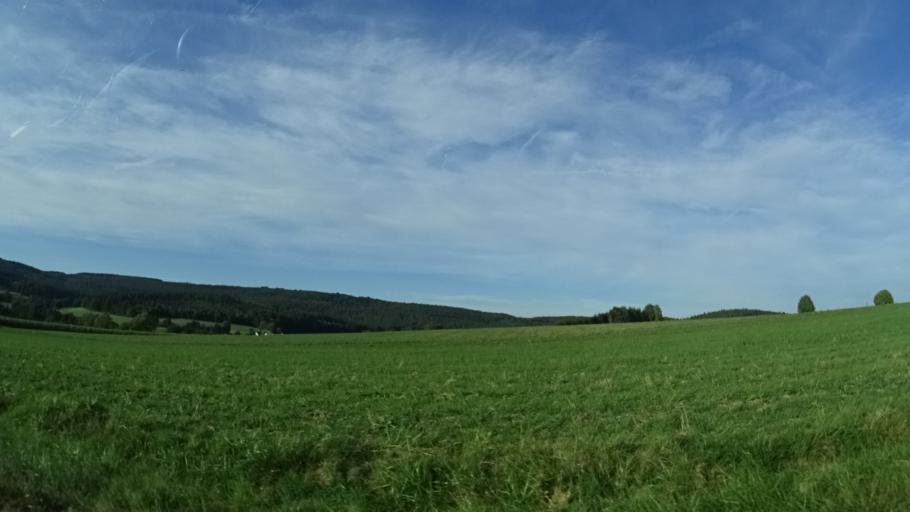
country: DE
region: Hesse
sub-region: Regierungsbezirk Kassel
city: Flieden
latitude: 50.4242
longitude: 9.5418
